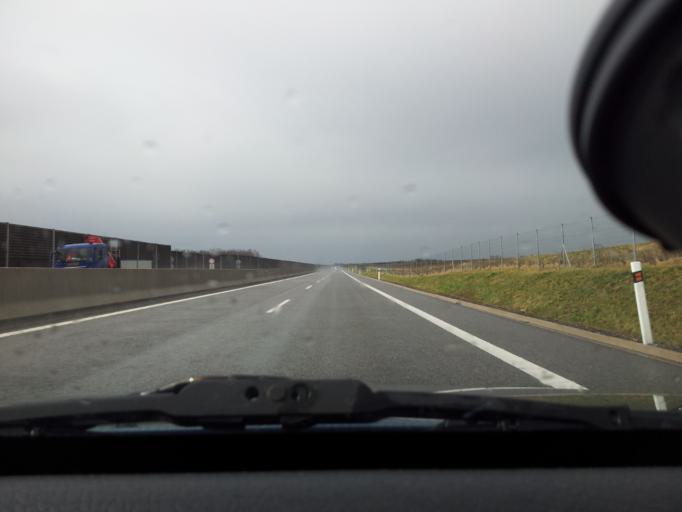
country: SK
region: Nitriansky
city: Zlate Moravce
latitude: 48.3469
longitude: 18.3529
